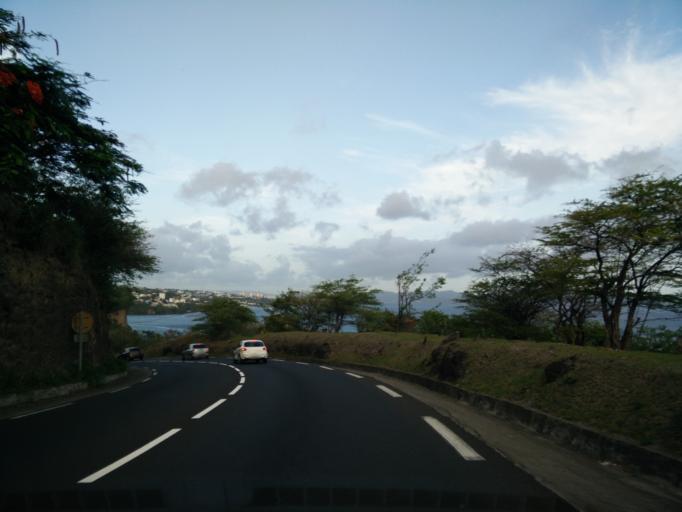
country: MQ
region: Martinique
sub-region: Martinique
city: Fort-de-France
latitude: 14.6301
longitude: -61.1230
